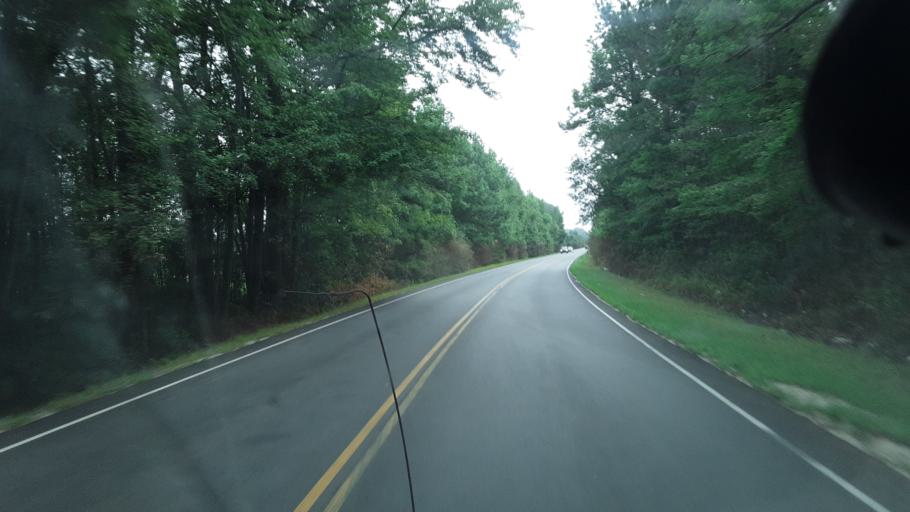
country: US
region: South Carolina
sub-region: Florence County
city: Johnsonville
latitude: 33.8948
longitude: -79.4464
